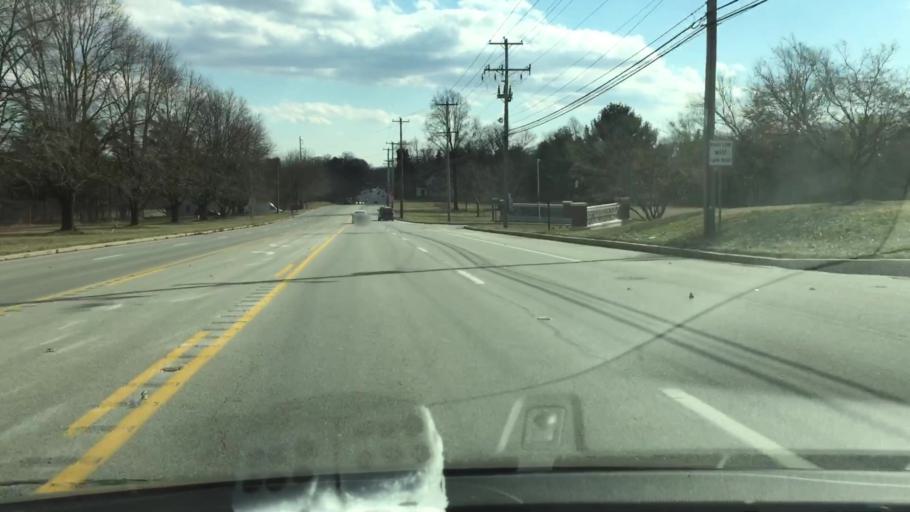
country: US
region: Pennsylvania
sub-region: Delaware County
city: Lima
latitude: 39.9101
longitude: -75.4201
